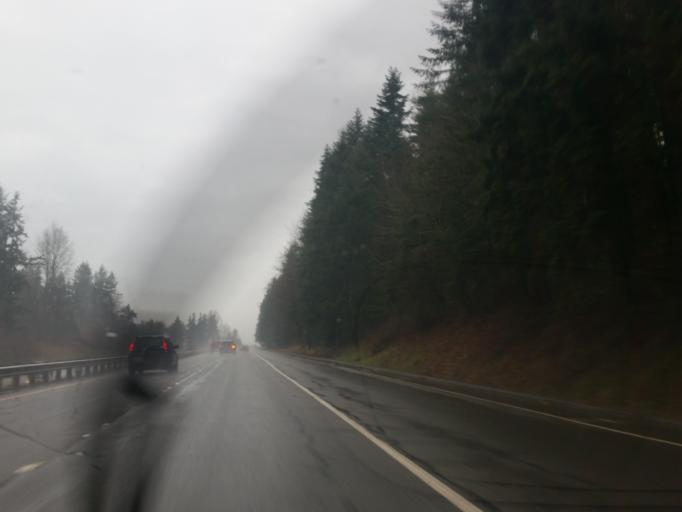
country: US
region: Washington
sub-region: Snohomish County
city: Maltby
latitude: 47.7875
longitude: -122.1376
